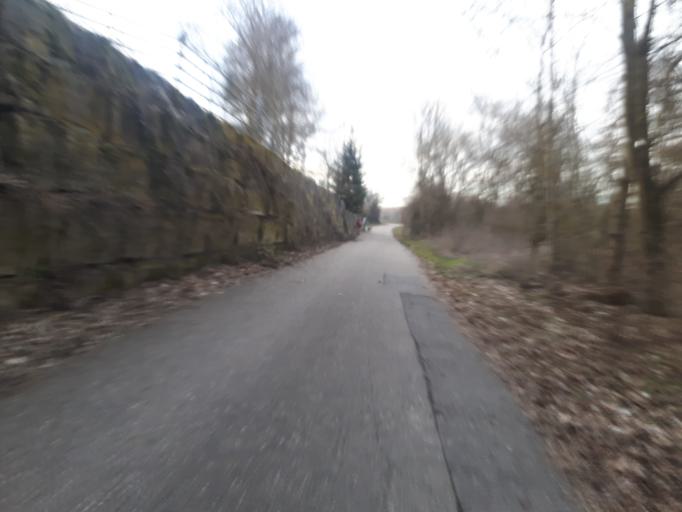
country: DE
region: Baden-Wuerttemberg
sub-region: Regierungsbezirk Stuttgart
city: Oedheim
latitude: 49.2543
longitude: 9.2881
